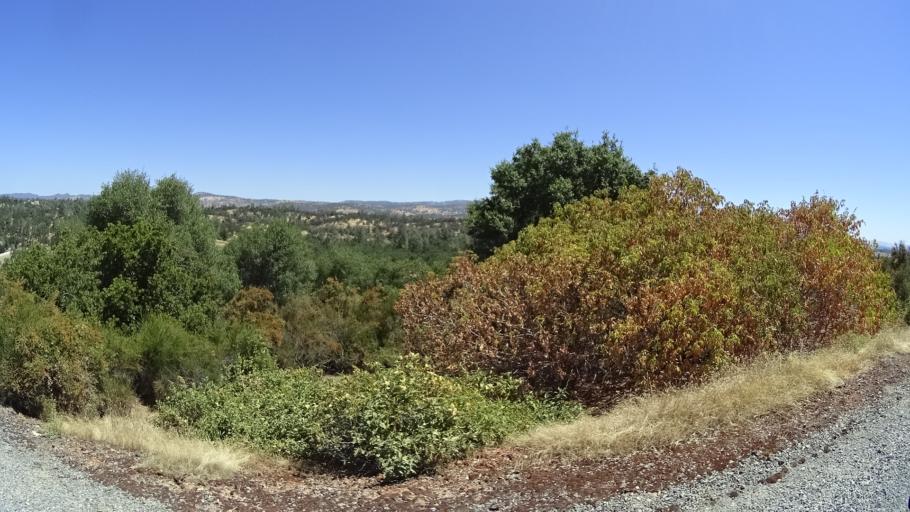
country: US
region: California
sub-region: Calaveras County
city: Copperopolis
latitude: 37.9588
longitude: -120.7000
